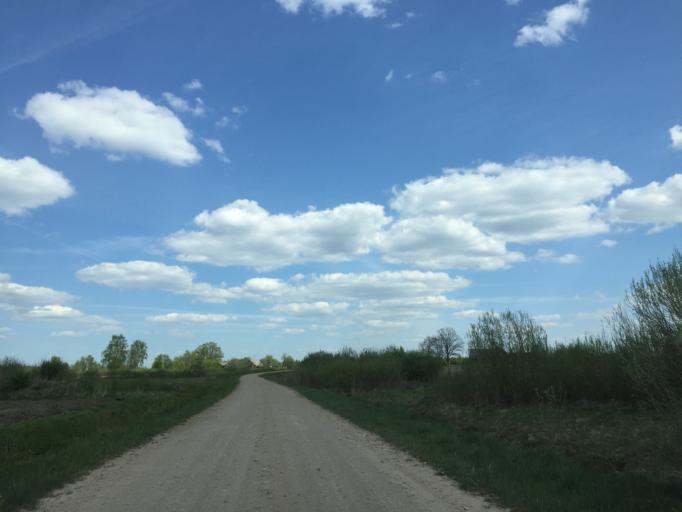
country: LV
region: Limbazu Rajons
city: Limbazi
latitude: 57.3833
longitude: 24.6569
